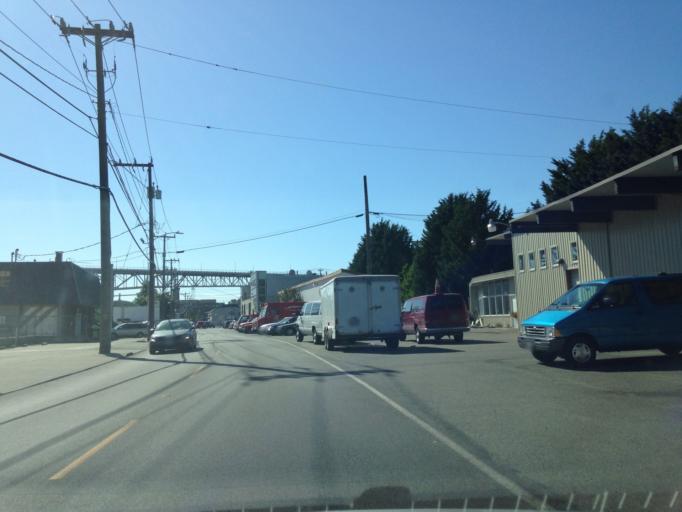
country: US
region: Washington
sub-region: King County
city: Seattle
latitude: 47.6477
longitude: -122.3405
